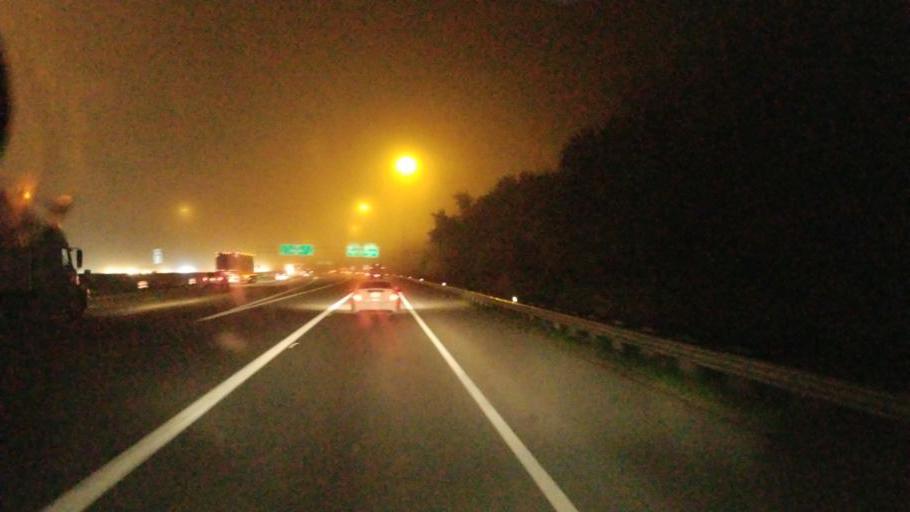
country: US
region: Ohio
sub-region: Franklin County
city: Obetz
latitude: 39.8778
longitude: -83.0129
